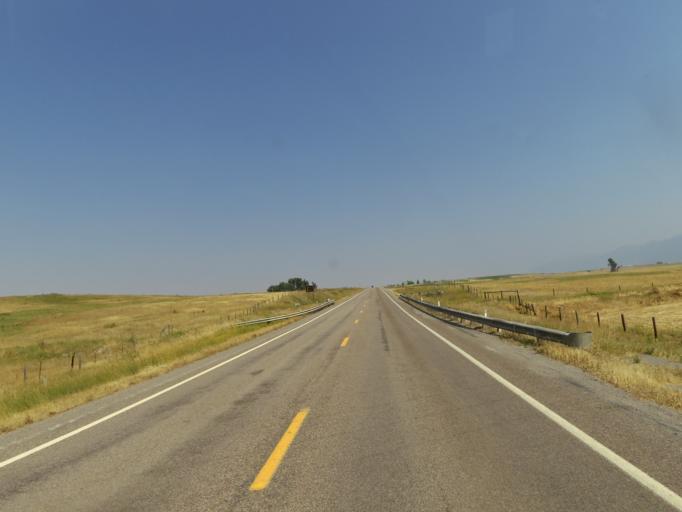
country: US
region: Montana
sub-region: Lake County
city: Ronan
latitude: 47.4072
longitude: -114.0969
